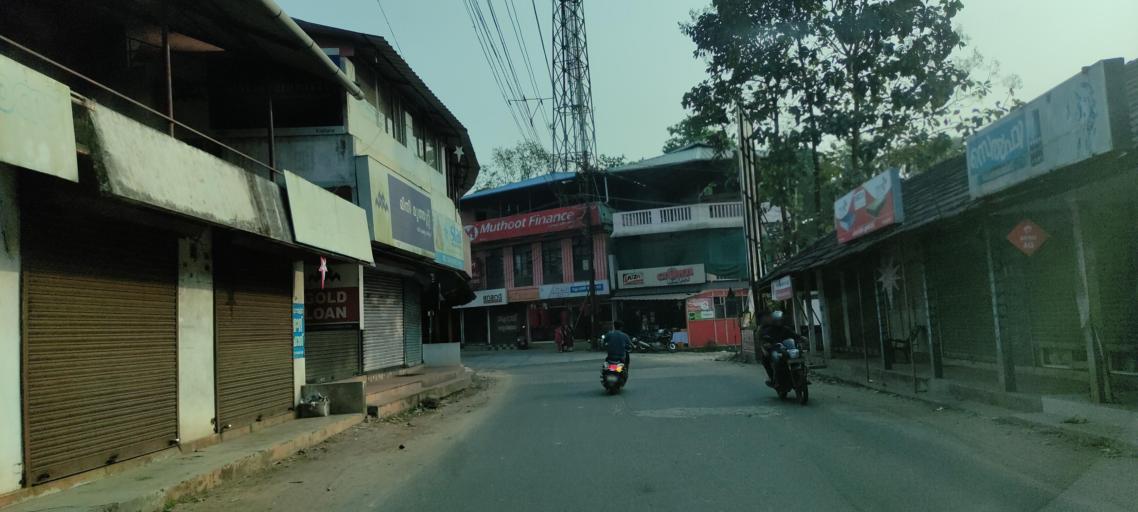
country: IN
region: Kerala
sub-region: Kottayam
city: Vaikam
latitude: 9.6987
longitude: 76.4776
